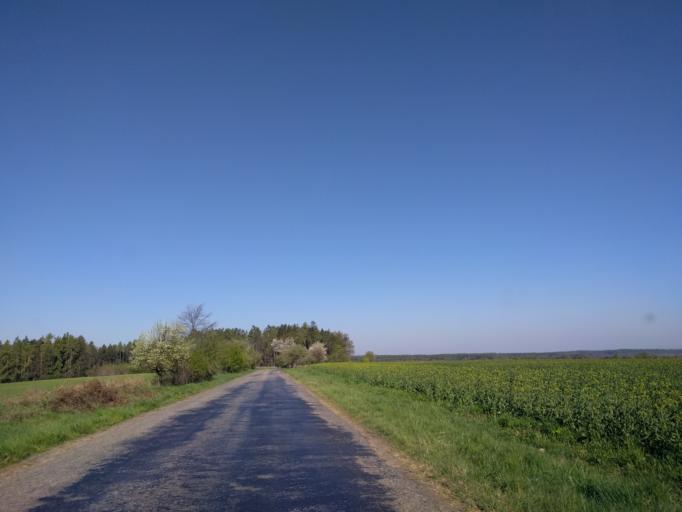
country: CZ
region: Central Bohemia
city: Mukarov
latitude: 49.9927
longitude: 14.7776
